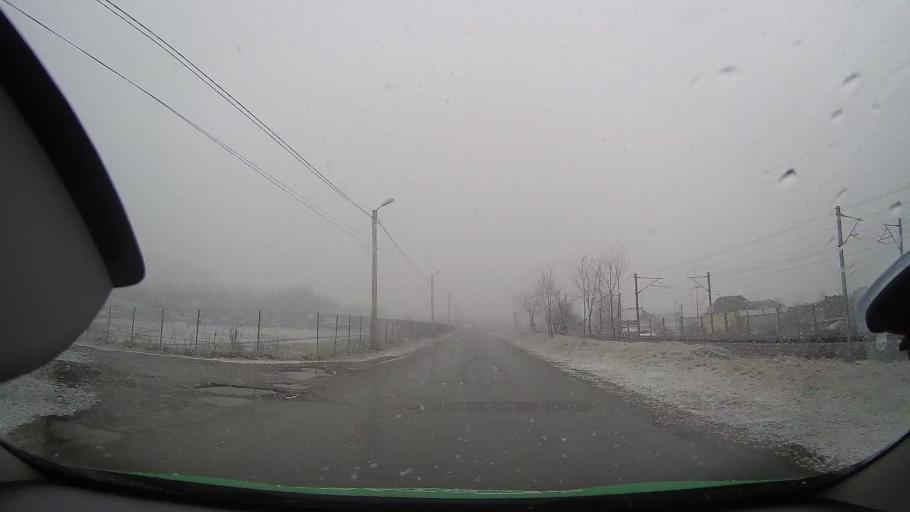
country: RO
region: Sibiu
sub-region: Municipiul Medias
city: Medias
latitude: 46.1662
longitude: 24.3688
